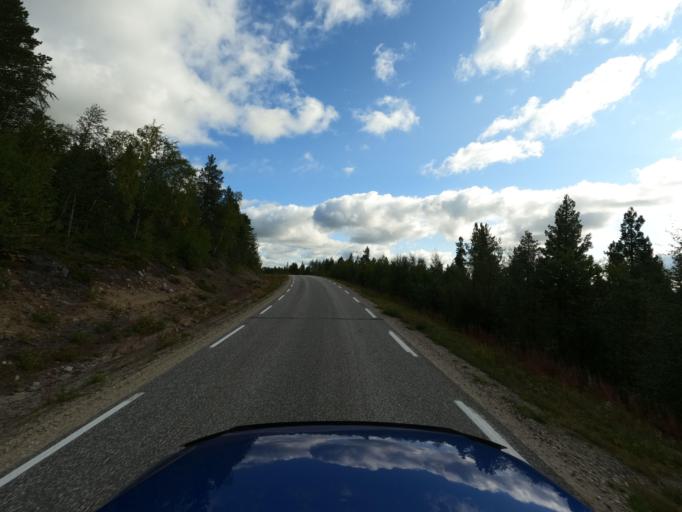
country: NO
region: Finnmark Fylke
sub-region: Karasjok
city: Karasjohka
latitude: 69.4424
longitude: 25.2560
